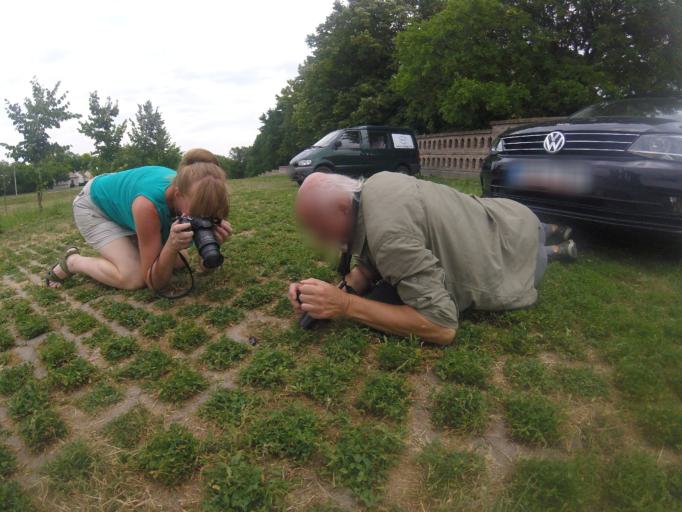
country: HU
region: Baranya
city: Boly
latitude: 45.9737
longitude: 18.5147
